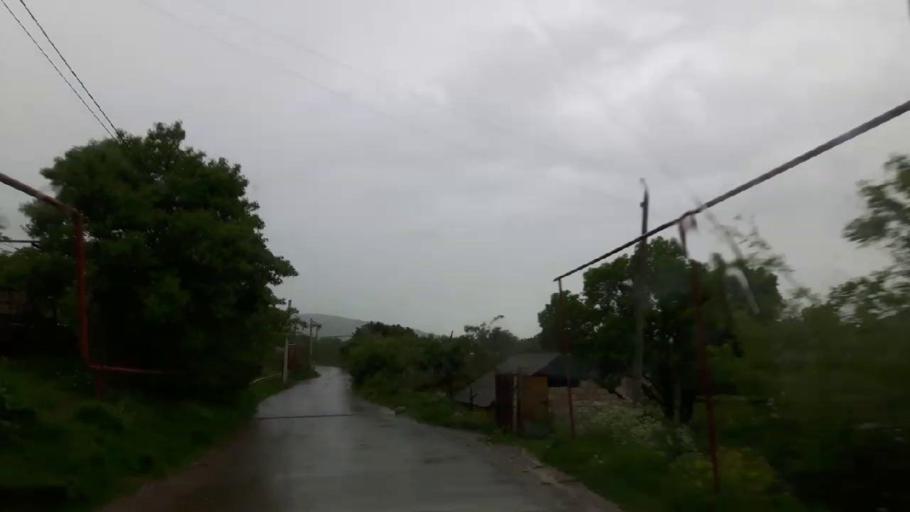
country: GE
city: Agara
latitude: 41.9843
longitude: 43.9257
